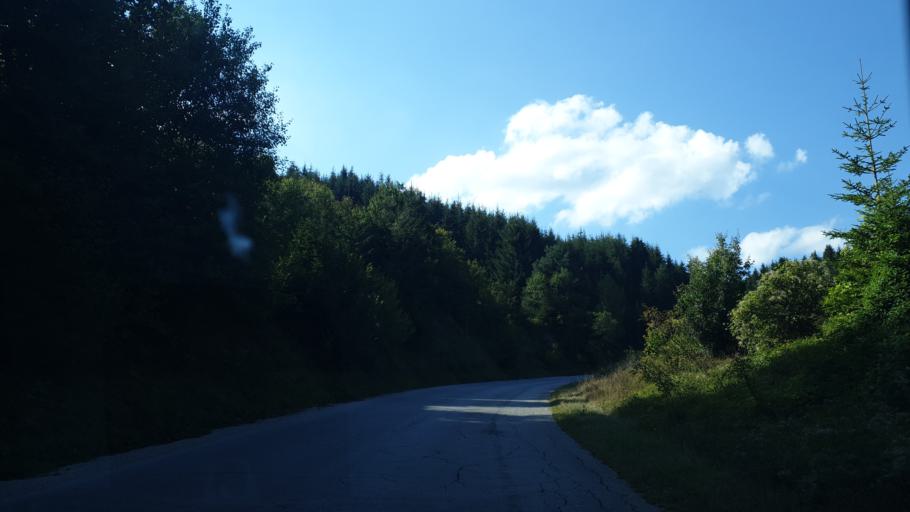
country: RS
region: Central Serbia
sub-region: Zlatiborski Okrug
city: Nova Varos
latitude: 43.4230
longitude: 19.9222
